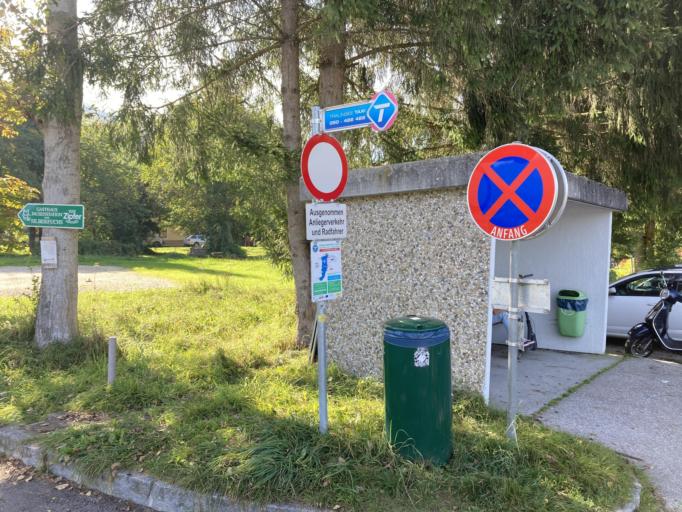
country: AT
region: Upper Austria
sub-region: Politischer Bezirk Gmunden
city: Gmunden
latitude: 47.9044
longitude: 13.8444
